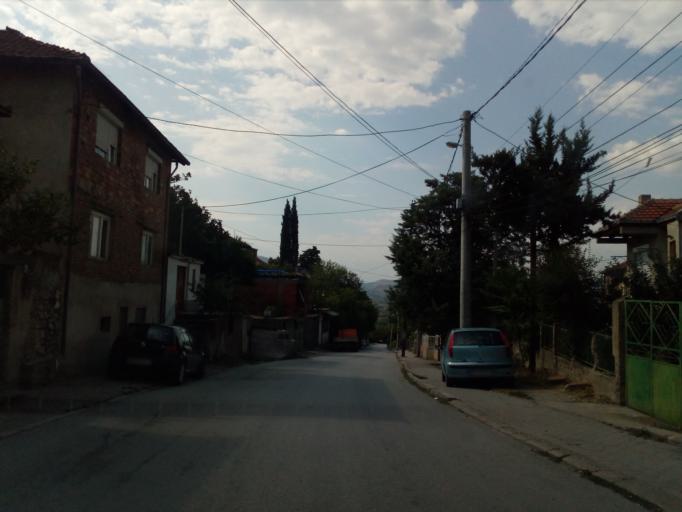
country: MK
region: Veles
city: Veles
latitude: 41.7144
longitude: 21.7792
